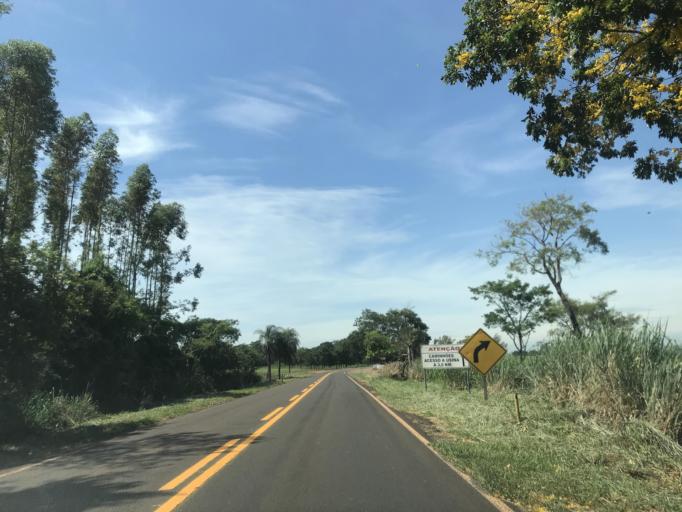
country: BR
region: Parana
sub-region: Terra Rica
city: Terra Rica
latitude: -22.7919
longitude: -52.6538
